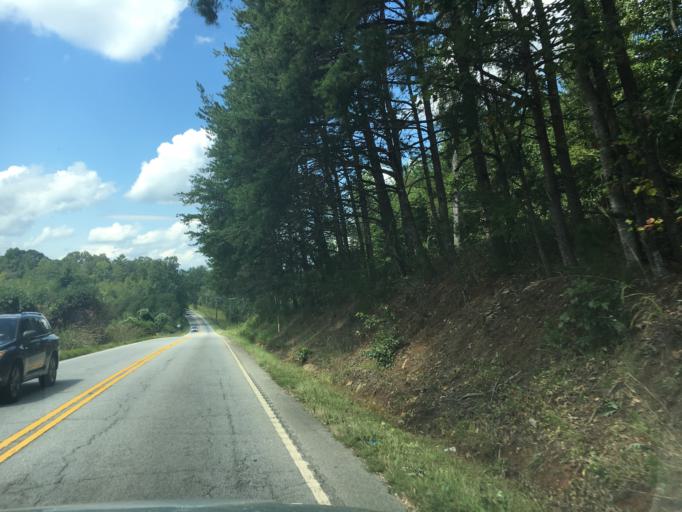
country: US
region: South Carolina
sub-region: Greenville County
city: Berea
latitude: 34.8886
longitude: -82.5263
